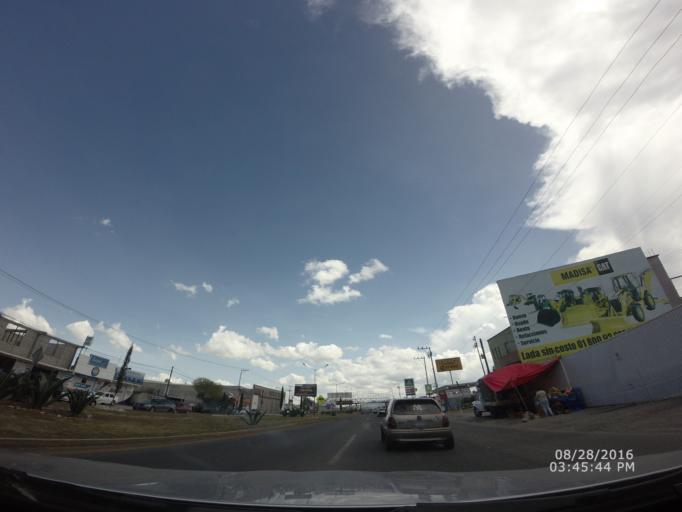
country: MX
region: Hidalgo
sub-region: Mineral de la Reforma
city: PRI Chacon
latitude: 20.0806
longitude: -98.7453
